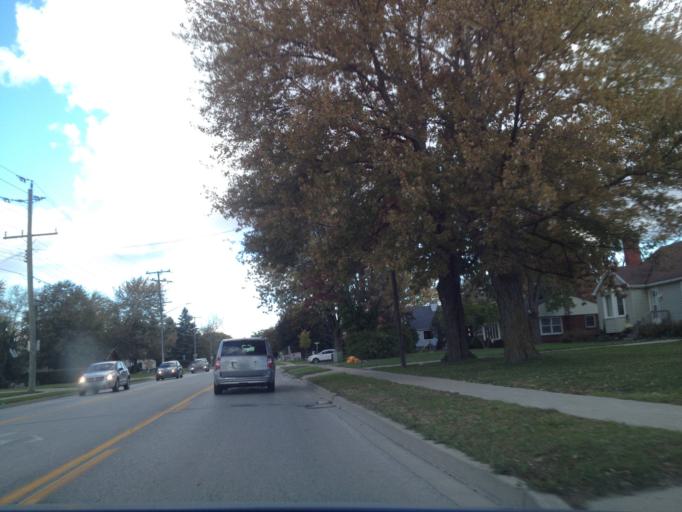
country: CA
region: Ontario
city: Amherstburg
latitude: 42.0446
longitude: -82.7391
